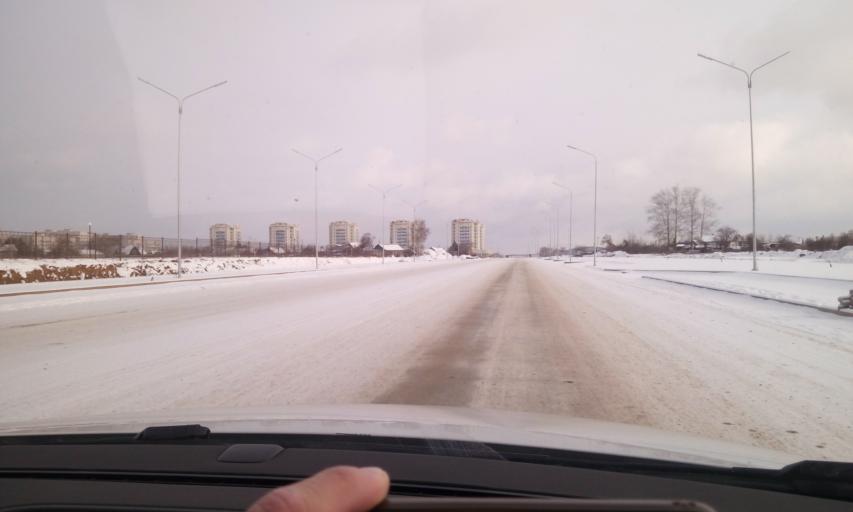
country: KZ
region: Astana Qalasy
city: Astana
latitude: 51.1207
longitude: 71.4947
